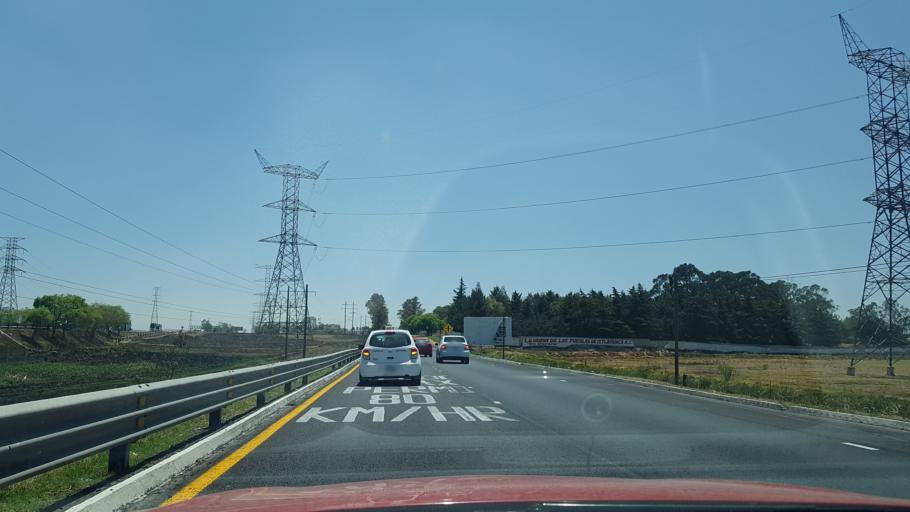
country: MX
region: Mexico
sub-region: Ixtlahuaca
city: Santo Domingo de Guzman
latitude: 19.6024
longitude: -99.7738
